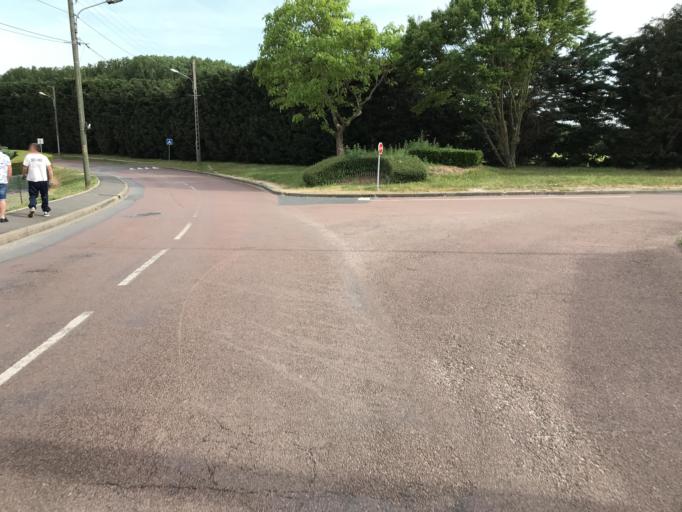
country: FR
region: Ile-de-France
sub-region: Departement de l'Essonne
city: Longpont-sur-Orge
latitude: 48.6269
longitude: 2.2910
